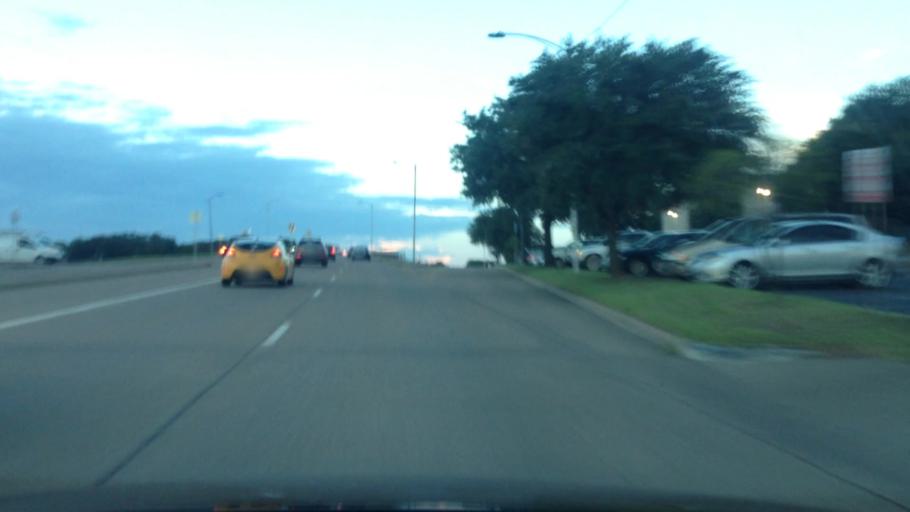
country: US
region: Texas
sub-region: Tarrant County
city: Arlington
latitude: 32.7385
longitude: -97.1319
